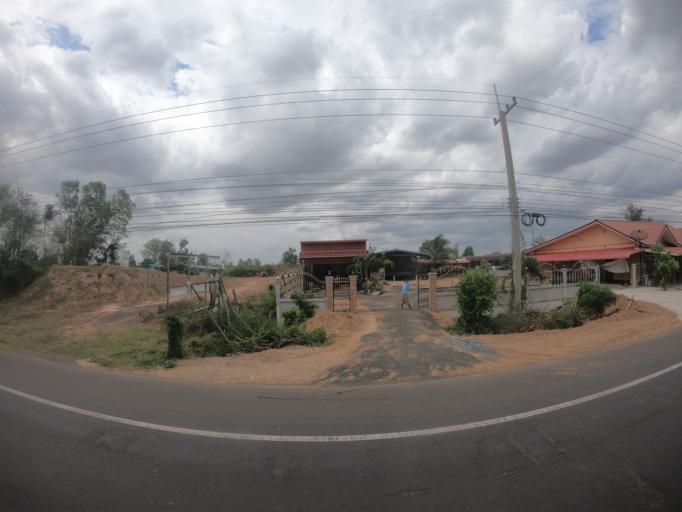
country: TH
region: Buriram
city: Nang Rong
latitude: 14.6368
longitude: 102.7063
